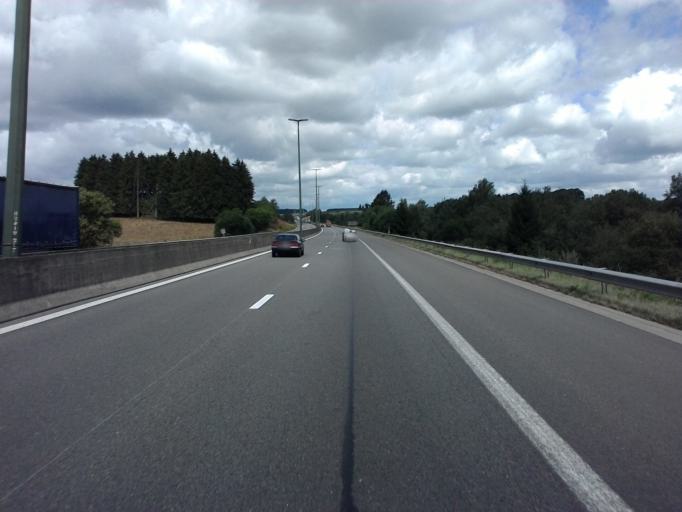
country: BE
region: Wallonia
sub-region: Province du Luxembourg
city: Leglise
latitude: 49.7679
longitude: 5.5560
